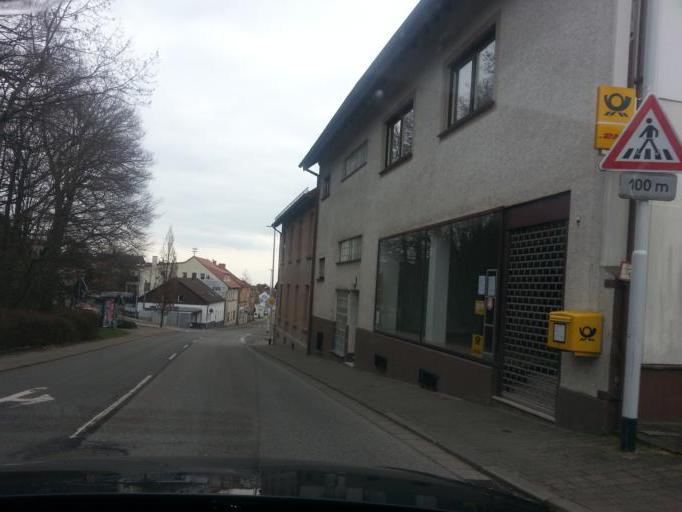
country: DE
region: Saarland
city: Bexbach
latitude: 49.3796
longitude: 7.2527
